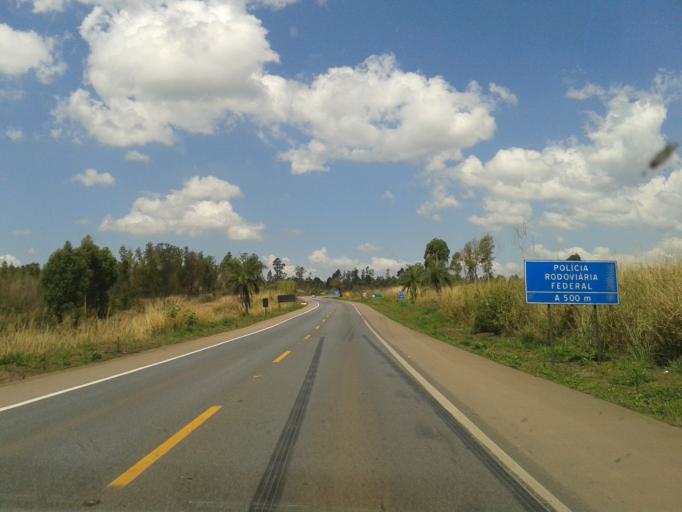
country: BR
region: Minas Gerais
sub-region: Campos Altos
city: Campos Altos
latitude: -19.6708
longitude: -46.0474
